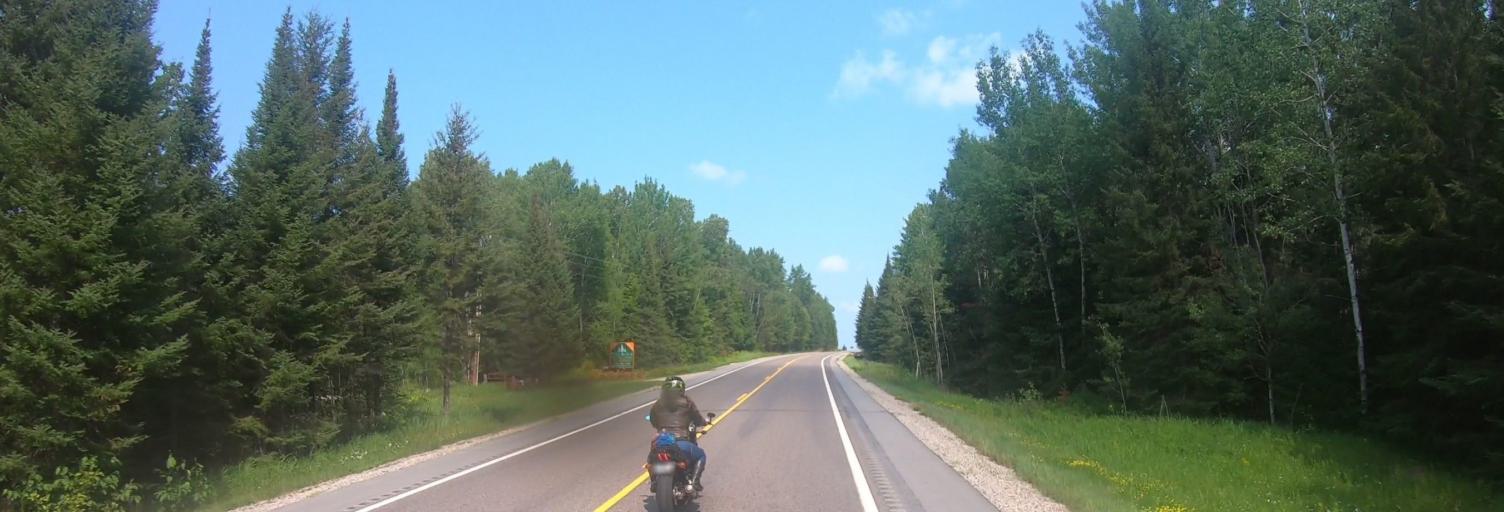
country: US
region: Minnesota
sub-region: Saint Louis County
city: Parkville
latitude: 48.1266
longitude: -92.5222
